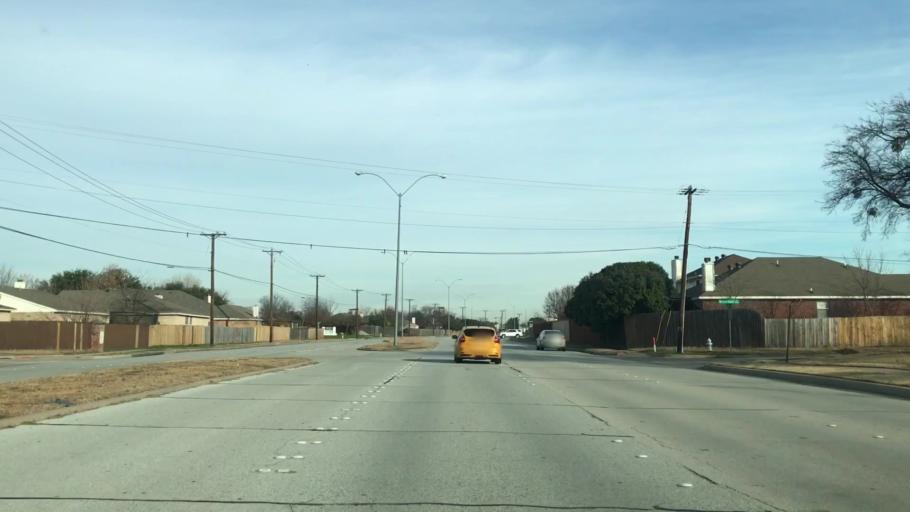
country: US
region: Texas
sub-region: Tarrant County
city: Watauga
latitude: 32.8683
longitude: -97.2912
